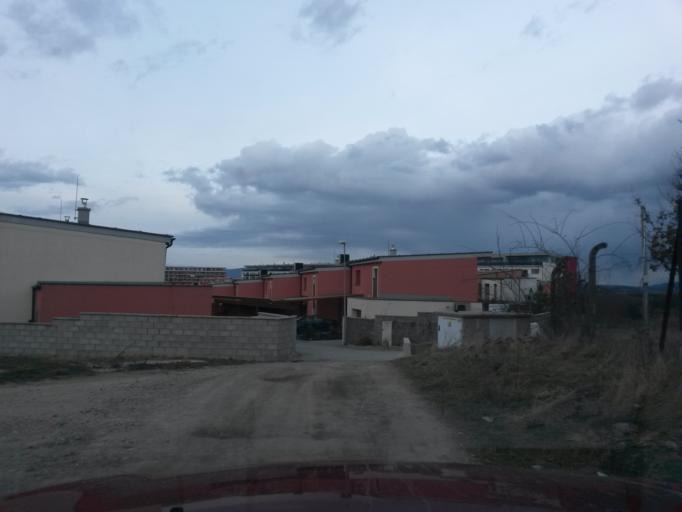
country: SK
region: Kosicky
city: Kosice
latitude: 48.7186
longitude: 21.2913
